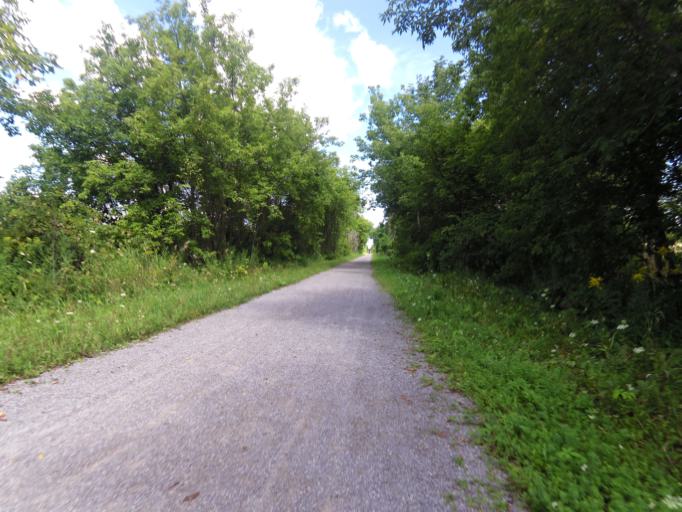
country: CA
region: Ontario
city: Ottawa
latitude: 45.3004
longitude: -75.6283
